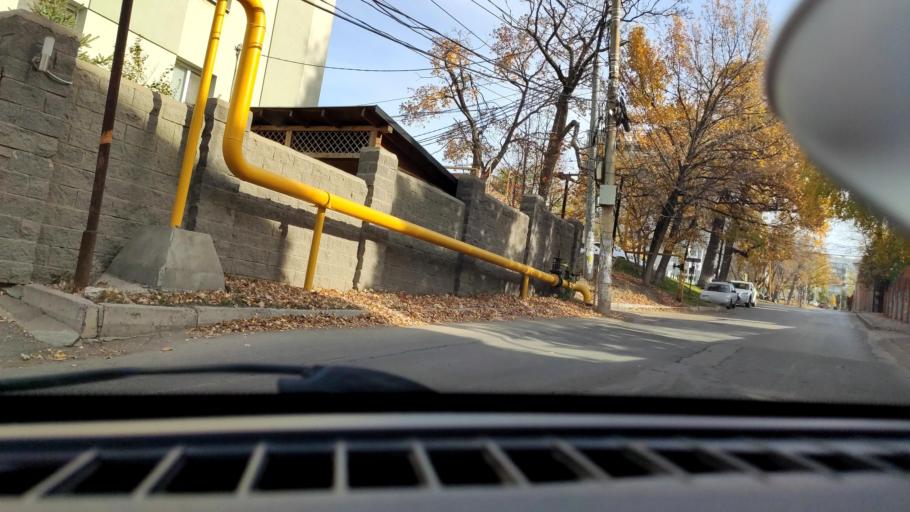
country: RU
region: Samara
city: Samara
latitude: 53.2599
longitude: 50.2016
